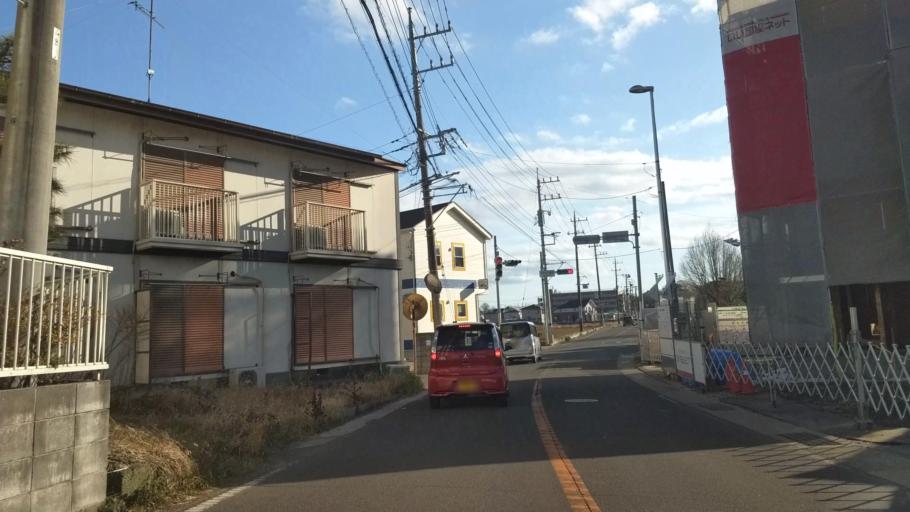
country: JP
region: Kanagawa
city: Isehara
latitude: 35.3761
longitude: 139.2829
